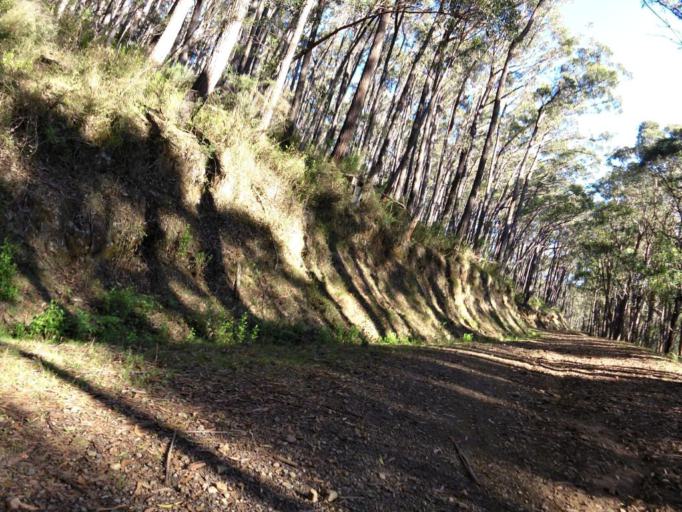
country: AU
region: Victoria
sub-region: Yarra Ranges
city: Millgrove
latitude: -37.7717
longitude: 145.6609
